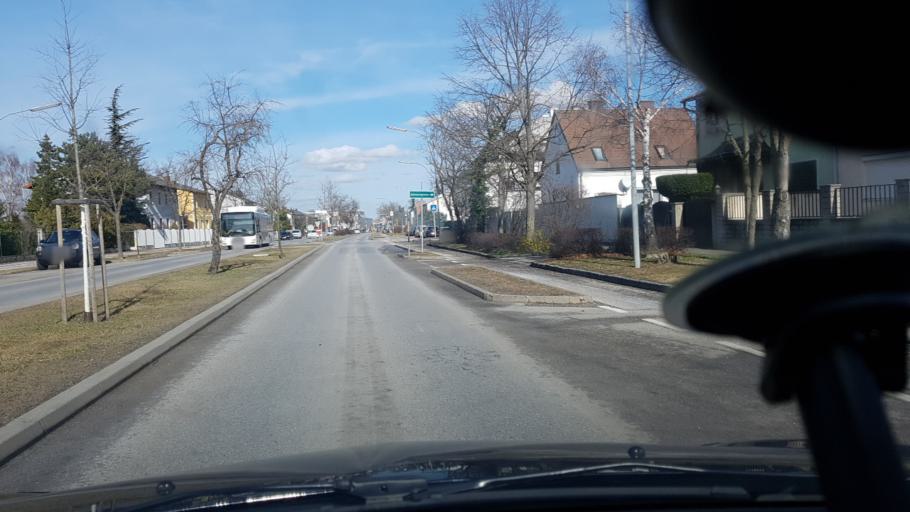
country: AT
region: Lower Austria
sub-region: Wiener Neustadt Stadt
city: Wiener Neustadt
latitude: 47.8127
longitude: 16.2163
